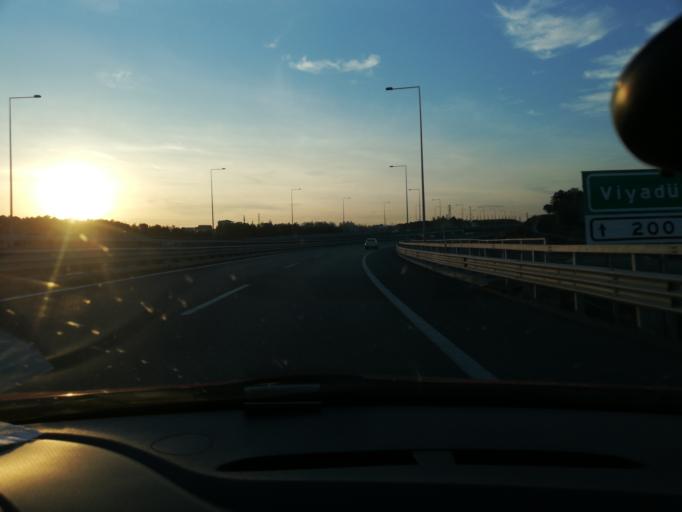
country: TR
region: Istanbul
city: Umraniye
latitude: 41.0495
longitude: 29.1278
